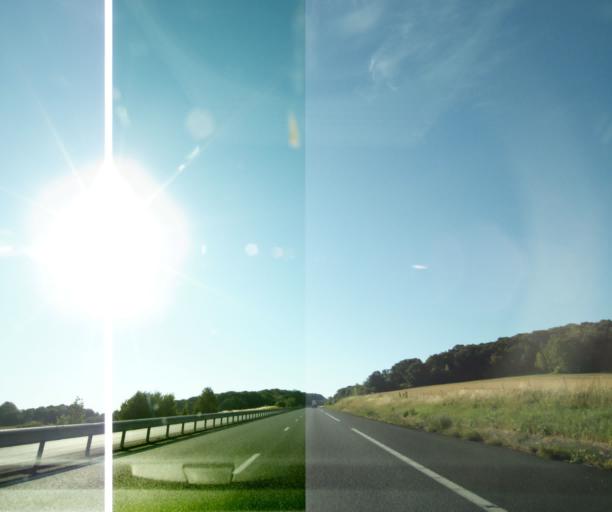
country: FR
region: Bourgogne
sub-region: Departement de l'Yonne
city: Soucy
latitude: 48.2441
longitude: 3.3537
